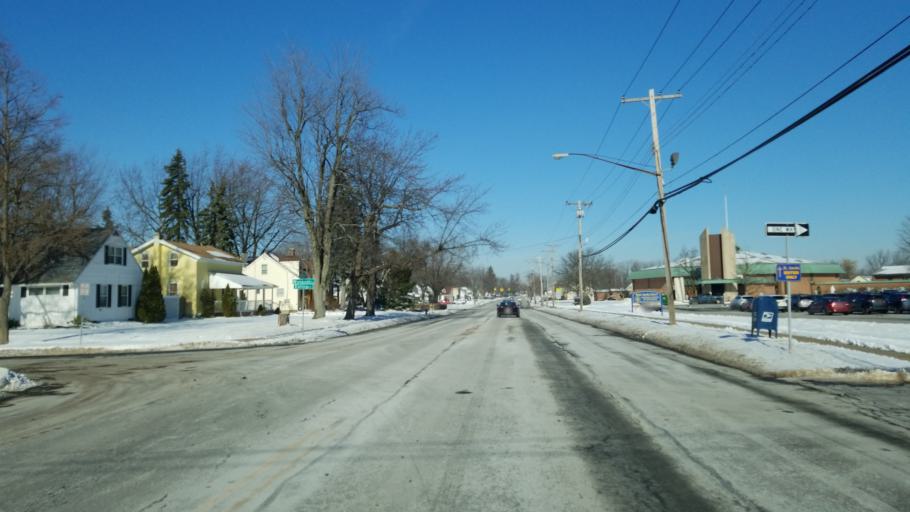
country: US
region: New York
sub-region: Erie County
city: Tonawanda
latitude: 42.9936
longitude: -78.8446
